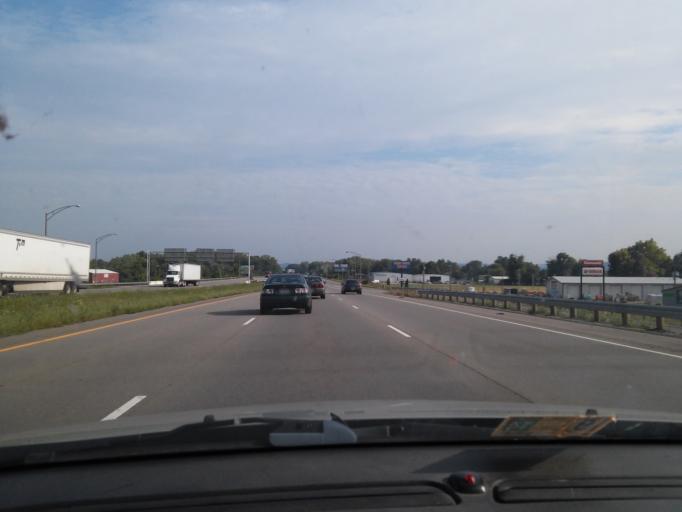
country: US
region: Ohio
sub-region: Ross County
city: Chillicothe
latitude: 39.3374
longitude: -82.9485
